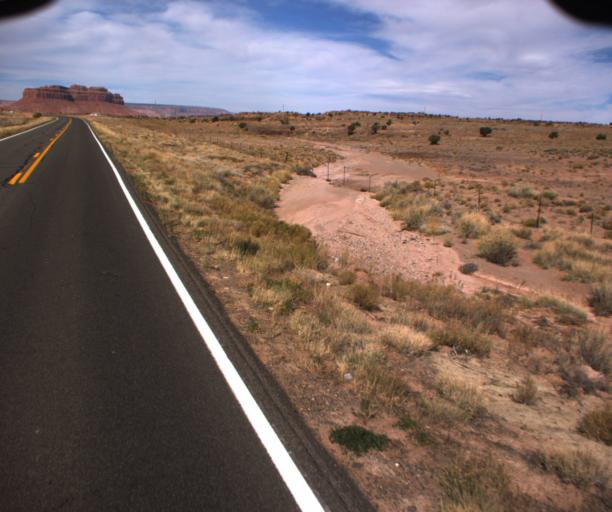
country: US
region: Arizona
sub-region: Navajo County
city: Kayenta
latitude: 36.8316
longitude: -110.2450
